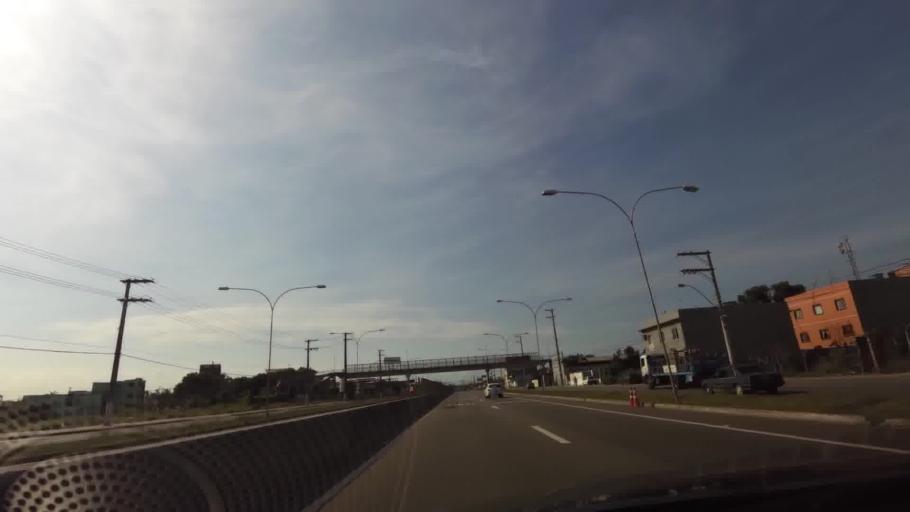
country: BR
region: Espirito Santo
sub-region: Vila Velha
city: Vila Velha
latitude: -20.4326
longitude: -40.3312
